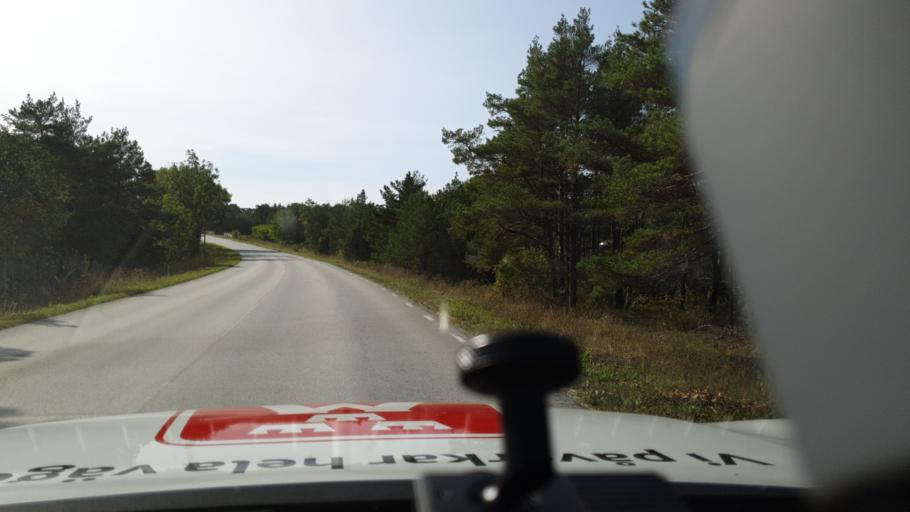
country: SE
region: Gotland
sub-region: Gotland
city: Slite
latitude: 57.9021
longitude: 19.0961
